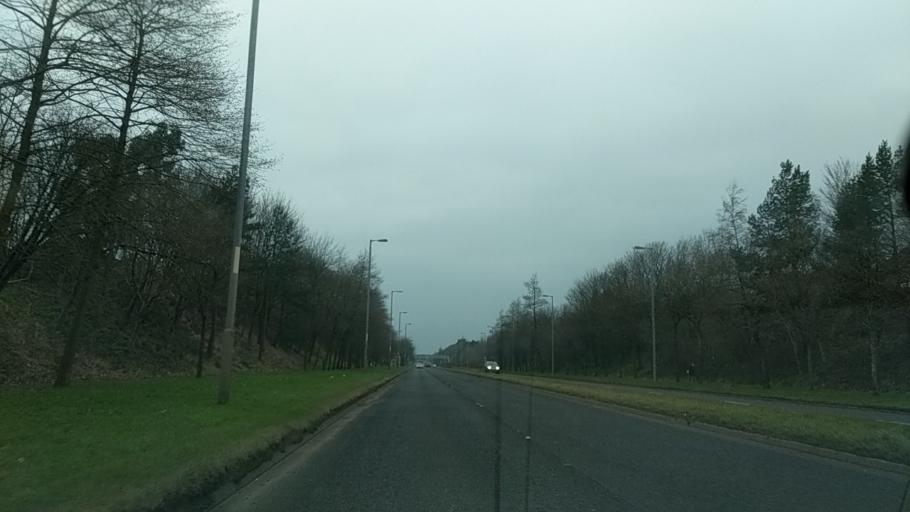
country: GB
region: Scotland
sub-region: South Lanarkshire
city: East Kilbride
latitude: 55.7612
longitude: -4.1918
